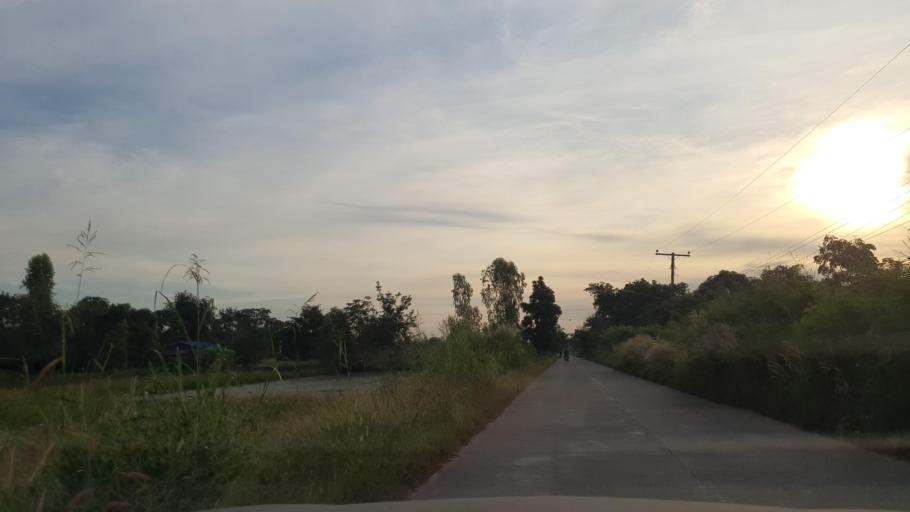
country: TH
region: Nakhon Sawan
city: Krok Phra
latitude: 15.6632
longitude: 100.0074
